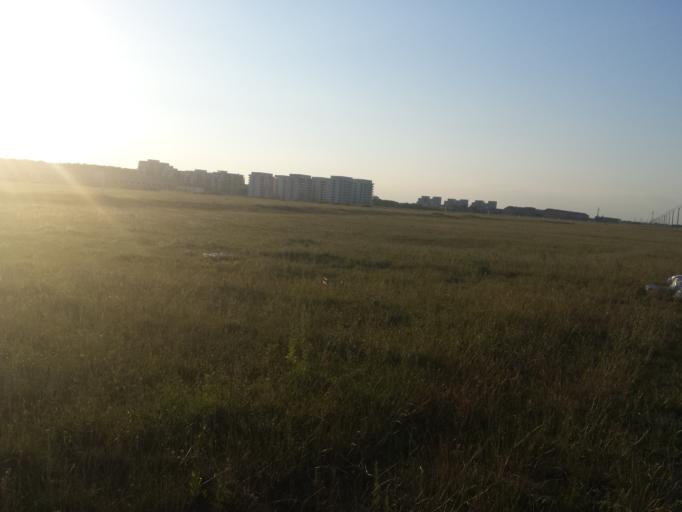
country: RO
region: Ilfov
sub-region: Comuna Tunari
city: Tunari
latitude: 44.5169
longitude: 26.1527
